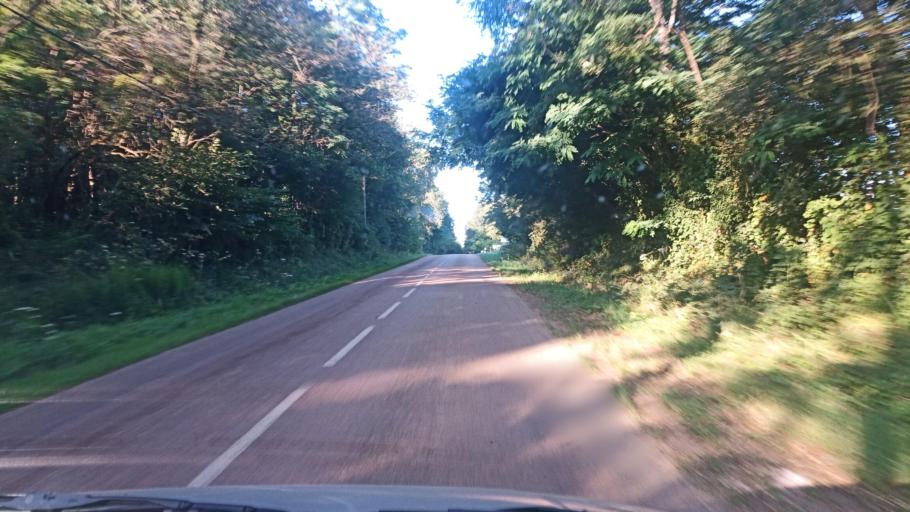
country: FR
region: Bourgogne
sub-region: Departement de l'Yonne
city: Pont-sur-Yonne
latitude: 48.2397
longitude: 3.1397
